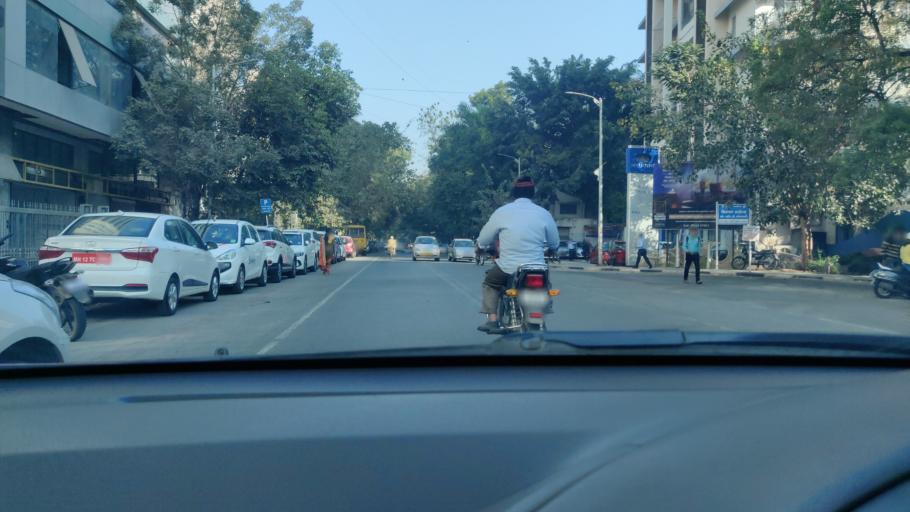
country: IN
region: Maharashtra
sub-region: Pune Division
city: Khadki
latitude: 18.5545
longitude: 73.8049
